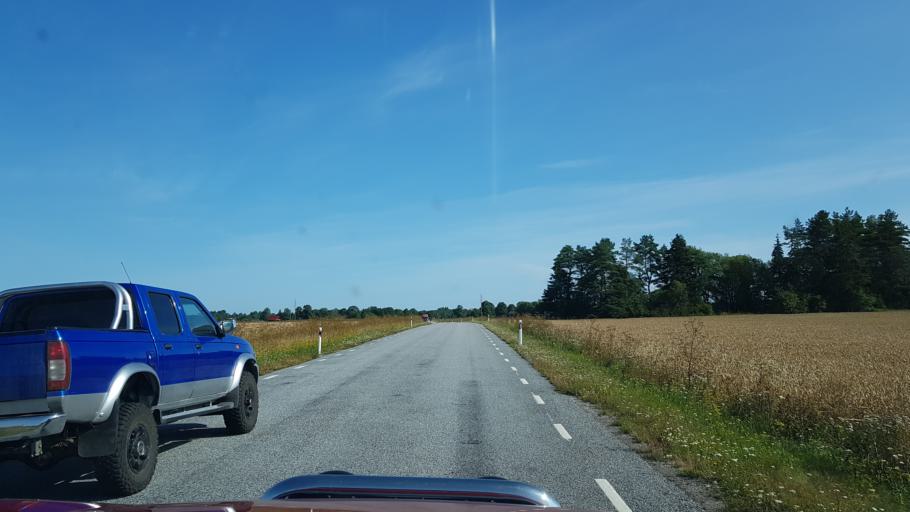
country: EE
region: Harju
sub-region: Raasiku vald
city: Raasiku
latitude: 59.2921
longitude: 25.1695
